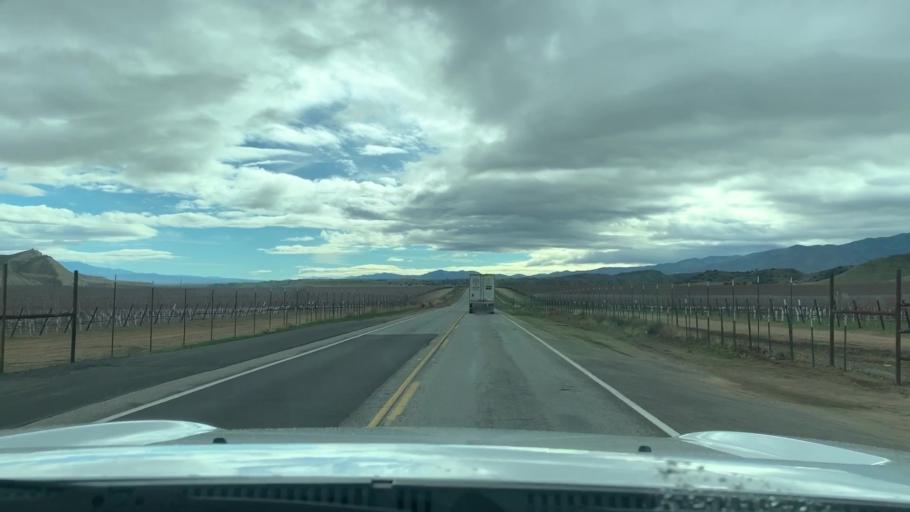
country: US
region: California
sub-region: Kern County
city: Taft Heights
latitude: 35.0172
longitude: -119.8533
